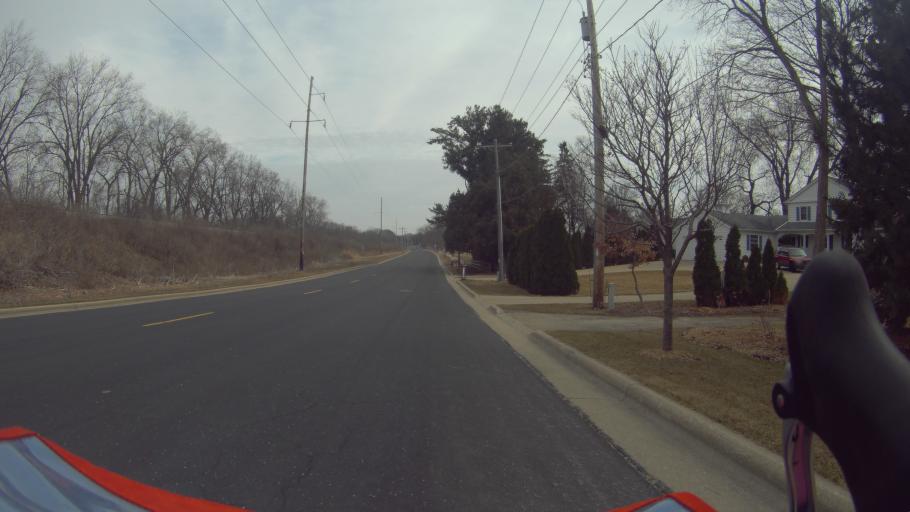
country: US
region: Wisconsin
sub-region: Dane County
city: Maple Bluff
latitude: 43.1296
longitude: -89.3803
